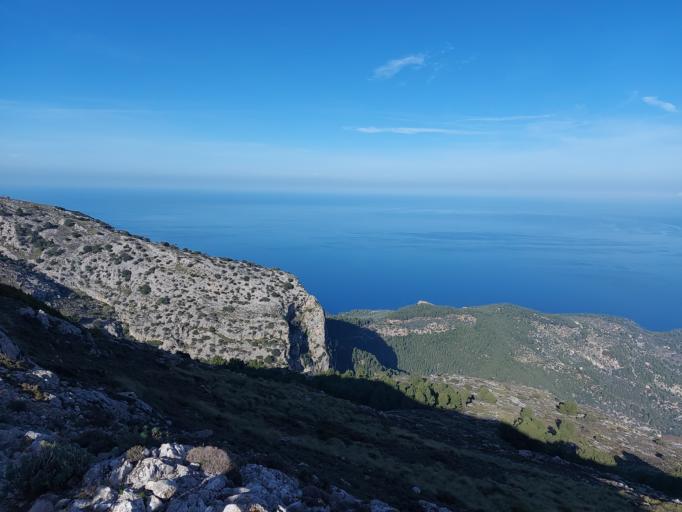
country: ES
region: Balearic Islands
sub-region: Illes Balears
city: Deia
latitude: 39.7325
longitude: 2.6482
